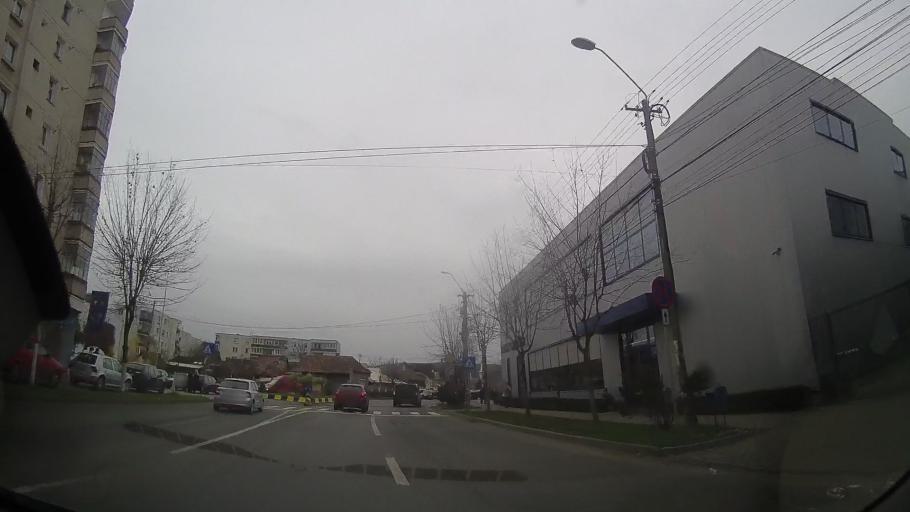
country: RO
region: Mures
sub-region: Comuna Santana de Mures
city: Santana de Mures
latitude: 46.5685
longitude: 24.5476
